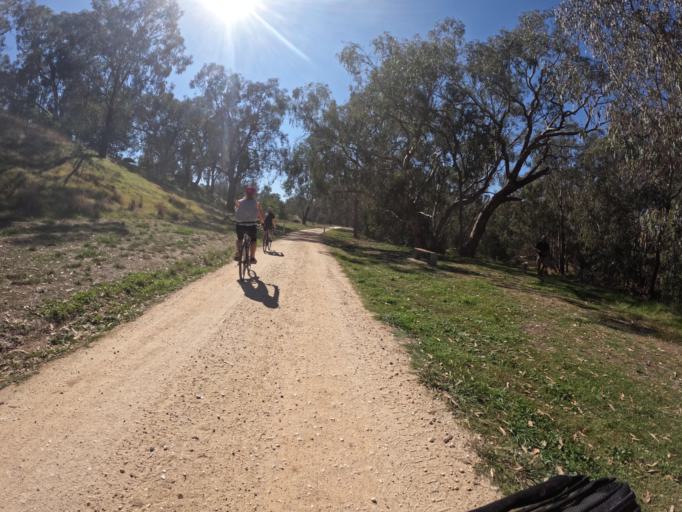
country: AU
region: Victoria
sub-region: Greater Bendigo
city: Epsom
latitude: -36.7930
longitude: 144.5051
